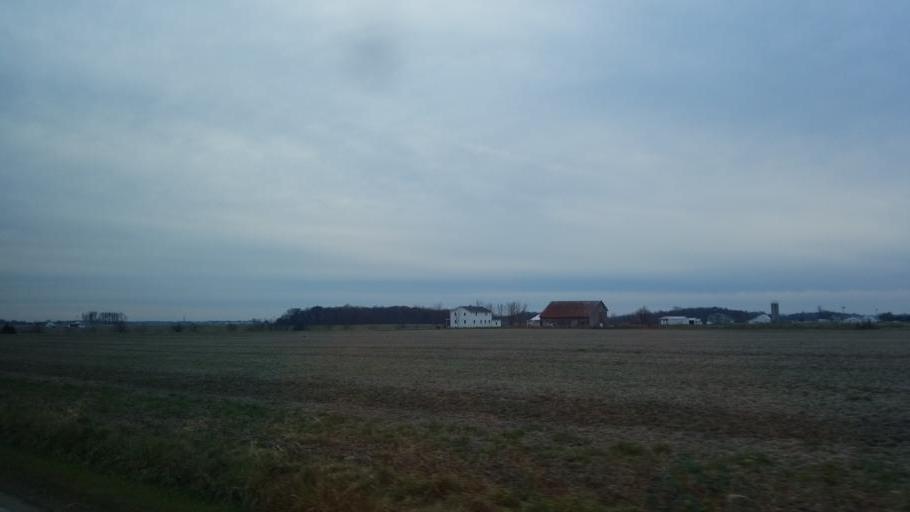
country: US
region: Indiana
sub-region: Adams County
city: Berne
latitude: 40.6969
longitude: -84.8792
